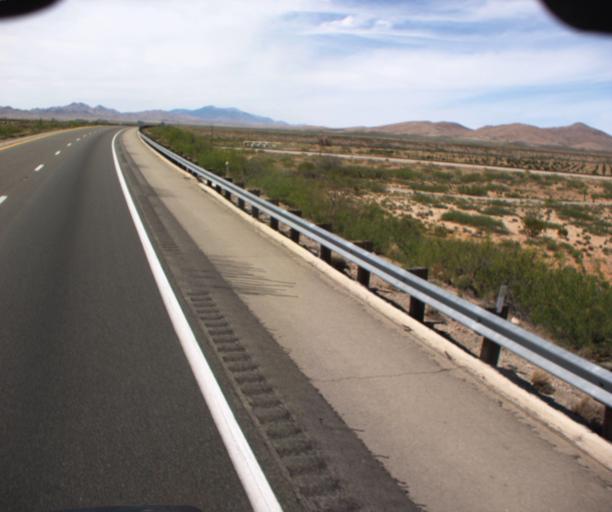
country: US
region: Arizona
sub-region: Cochise County
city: Willcox
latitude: 32.3505
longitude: -109.6062
